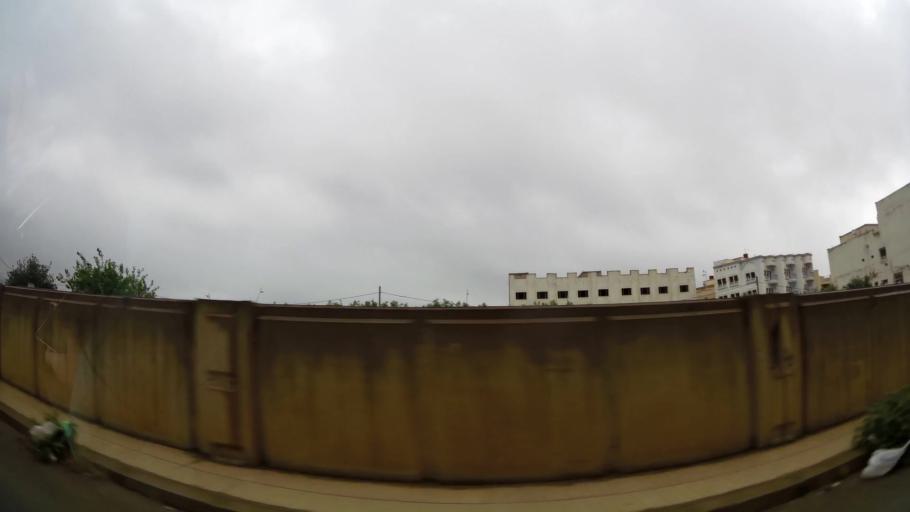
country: MA
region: Oriental
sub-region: Nador
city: Nador
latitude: 35.1610
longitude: -2.9660
